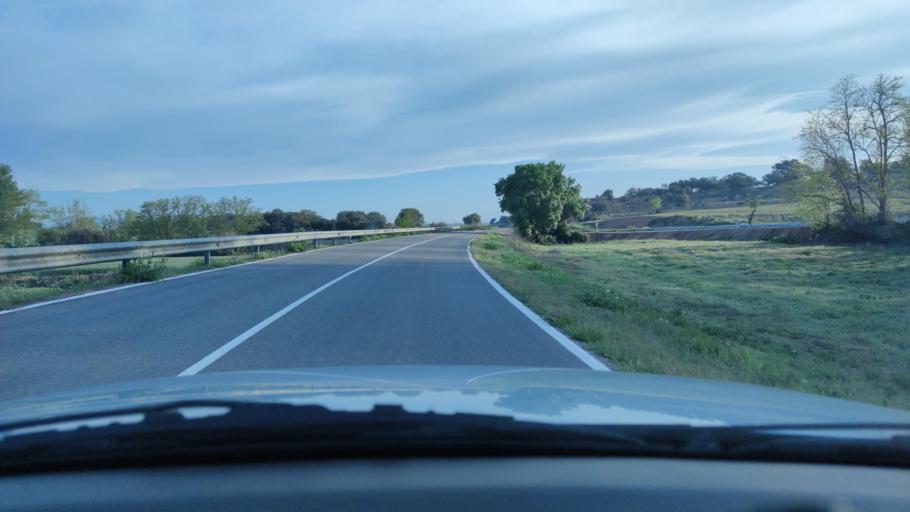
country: ES
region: Catalonia
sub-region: Provincia de Lleida
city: Agramunt
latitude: 41.8054
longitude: 1.0526
